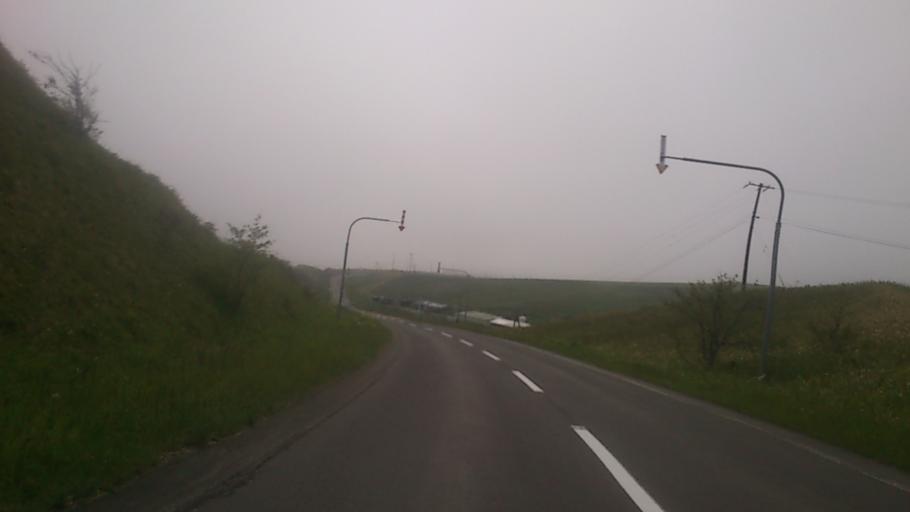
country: JP
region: Hokkaido
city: Nemuro
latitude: 43.1760
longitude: 145.3004
